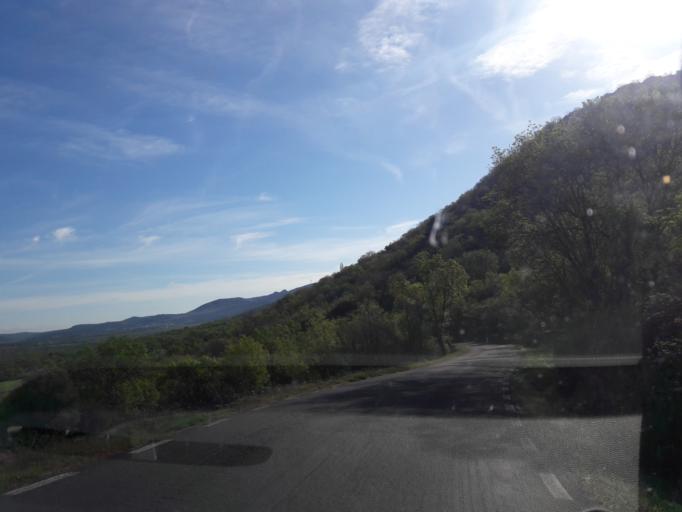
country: ES
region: Castille and Leon
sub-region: Provincia de Salamanca
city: Navalmoral de Bejar
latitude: 40.4283
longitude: -5.7823
